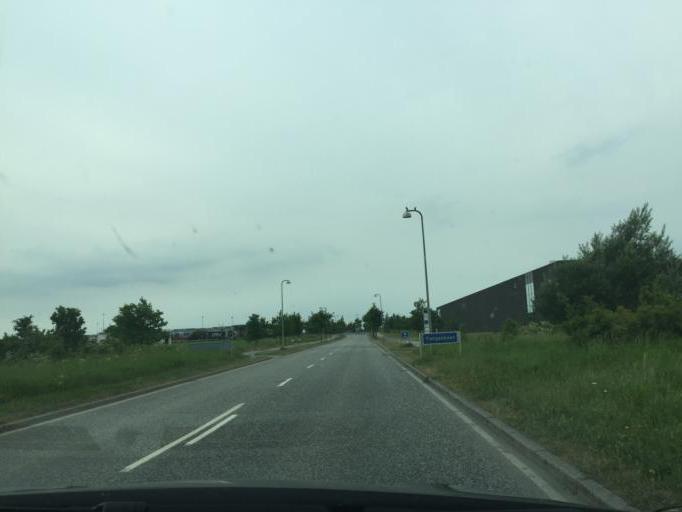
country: DK
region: South Denmark
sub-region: Odense Kommune
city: Neder Holluf
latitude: 55.3733
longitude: 10.4976
